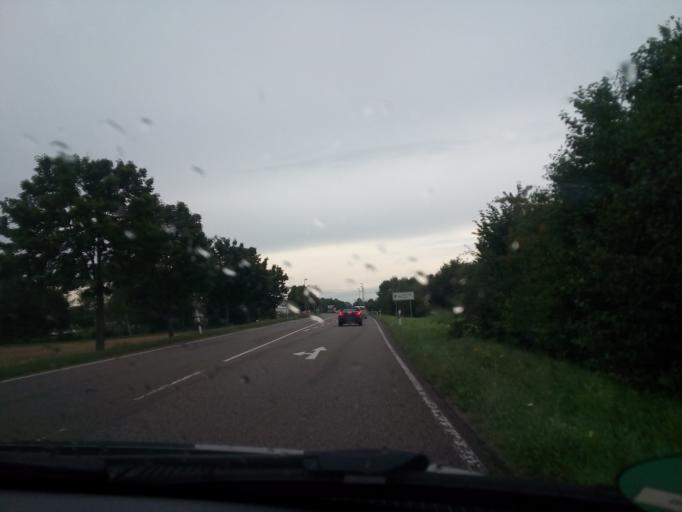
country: DE
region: Baden-Wuerttemberg
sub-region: Karlsruhe Region
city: Buhl
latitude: 48.6911
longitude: 8.1164
